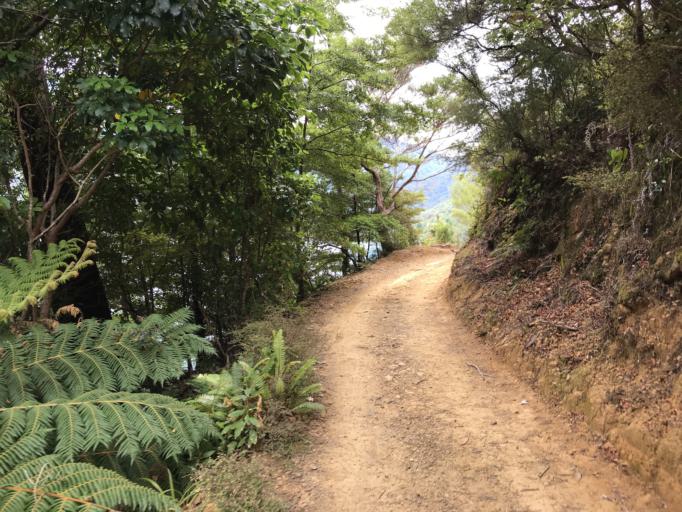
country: NZ
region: Marlborough
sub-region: Marlborough District
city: Picton
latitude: -41.0968
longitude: 174.1883
